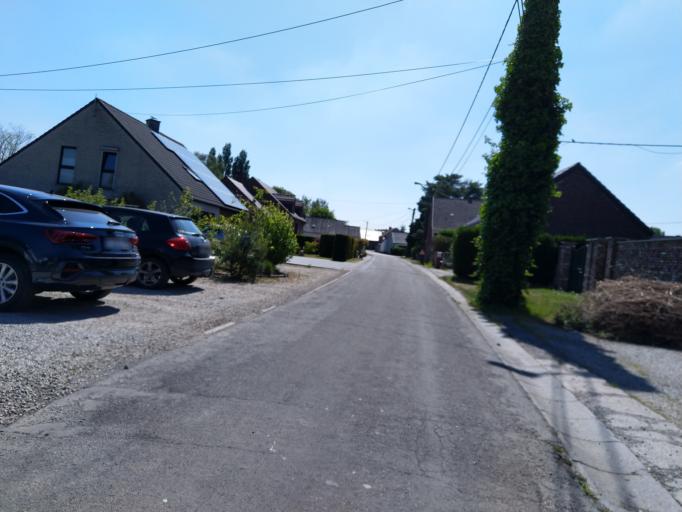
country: BE
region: Wallonia
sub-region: Province du Hainaut
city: Jurbise
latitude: 50.5091
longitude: 3.8697
